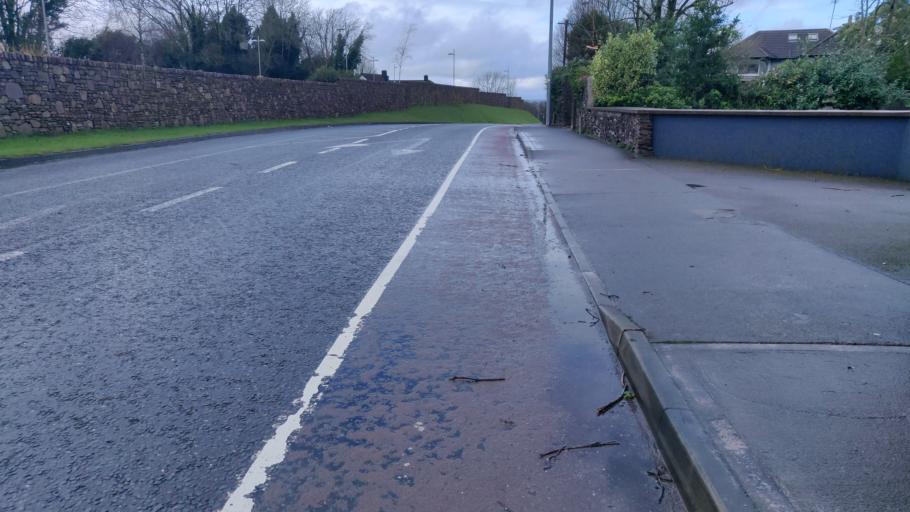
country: IE
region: Munster
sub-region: County Cork
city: Cork
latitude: 51.8707
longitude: -8.4185
